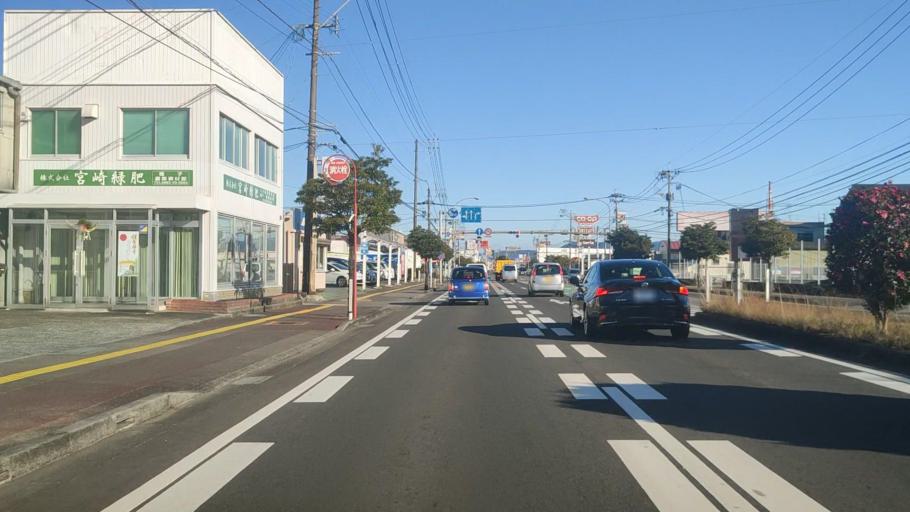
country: JP
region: Miyazaki
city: Nobeoka
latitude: 32.5576
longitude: 131.6800
